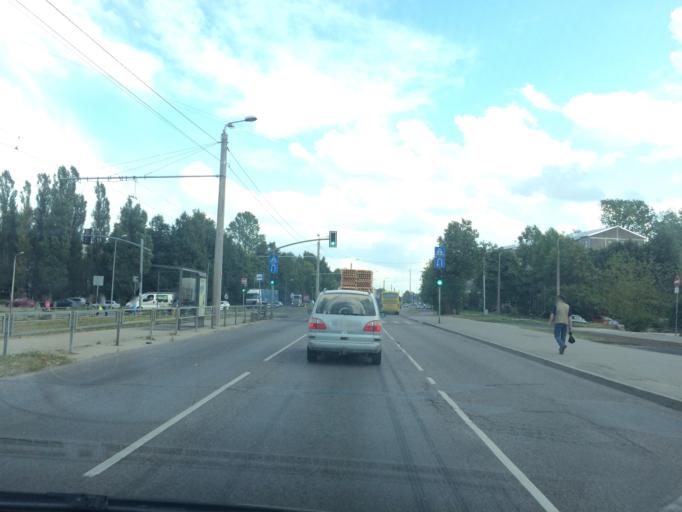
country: LV
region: Kekava
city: Balozi
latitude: 56.9086
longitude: 24.1830
